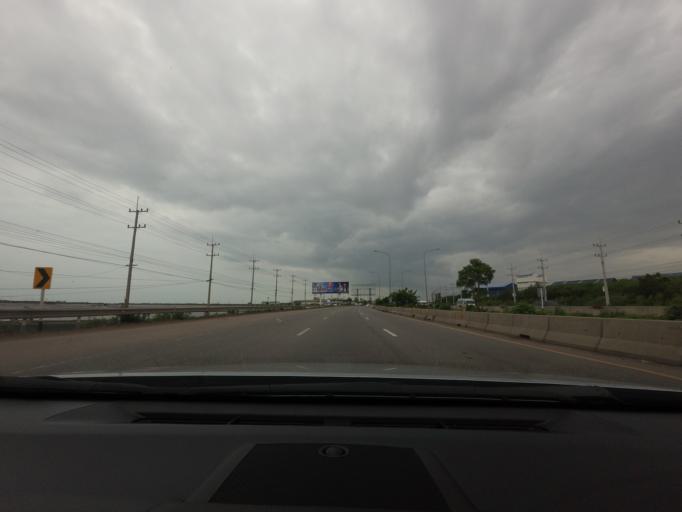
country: TH
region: Samut Sakhon
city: Ban Phaeo
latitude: 13.4777
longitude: 100.1183
